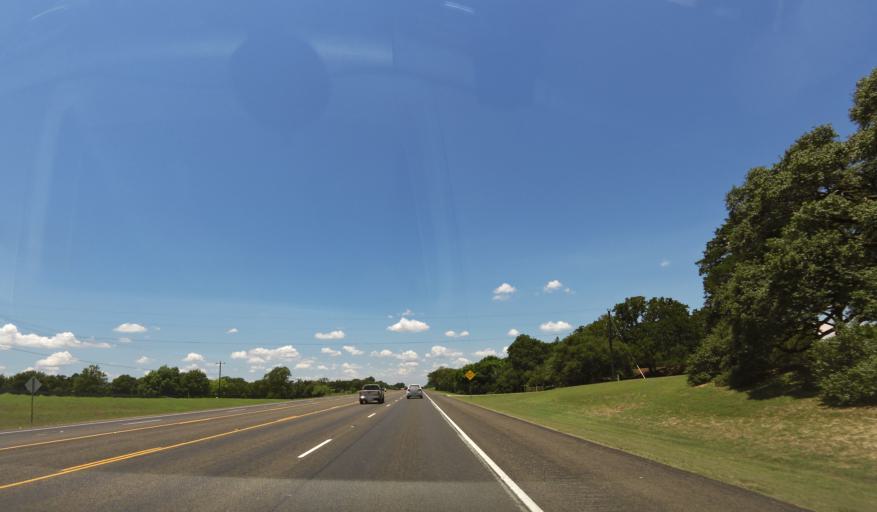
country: US
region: Texas
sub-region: Washington County
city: Brenham
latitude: 30.1779
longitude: -96.4667
